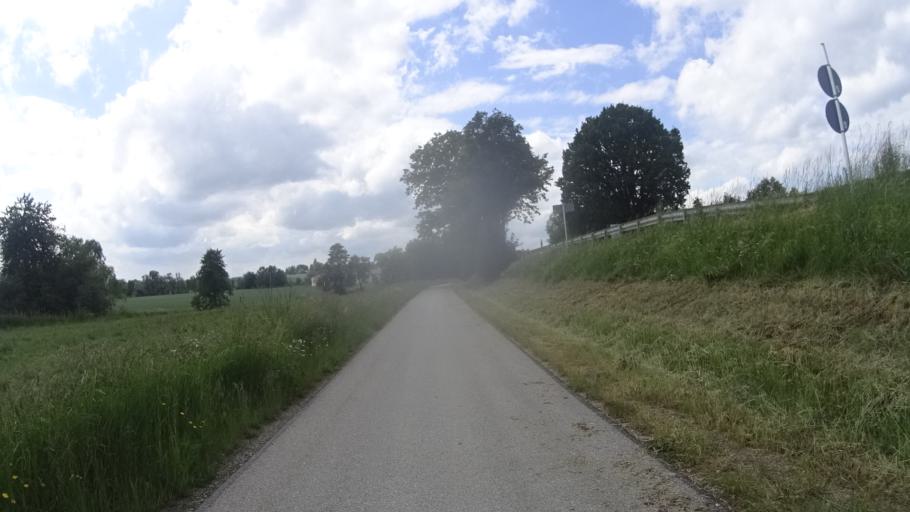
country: DE
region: Bavaria
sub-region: Lower Bavaria
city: Massing
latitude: 48.3955
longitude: 12.6371
